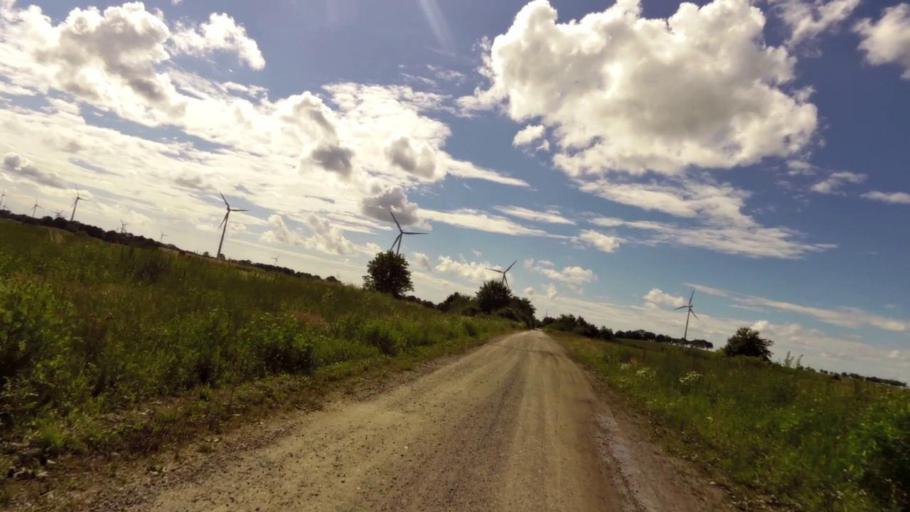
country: PL
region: Pomeranian Voivodeship
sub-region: Powiat slupski
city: Ustka
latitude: 54.5160
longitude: 16.7286
